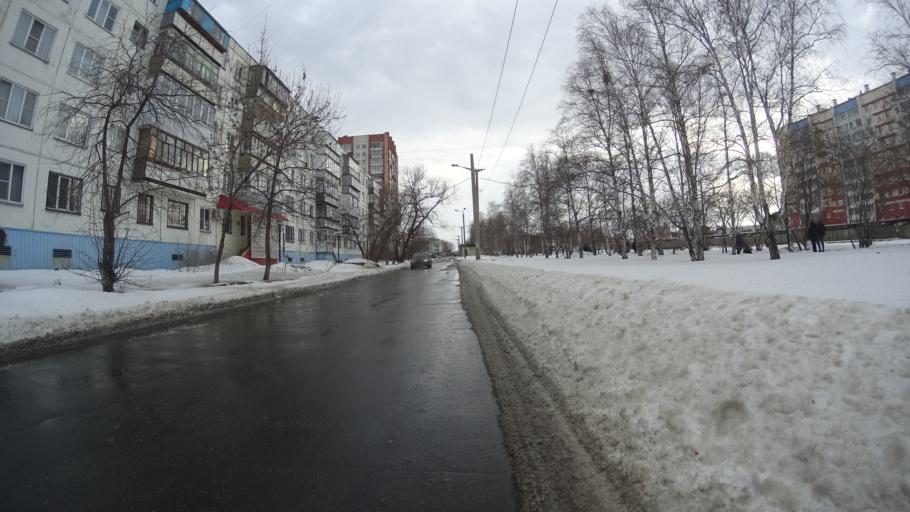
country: RU
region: Chelyabinsk
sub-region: Gorod Chelyabinsk
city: Chelyabinsk
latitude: 55.1965
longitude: 61.3223
